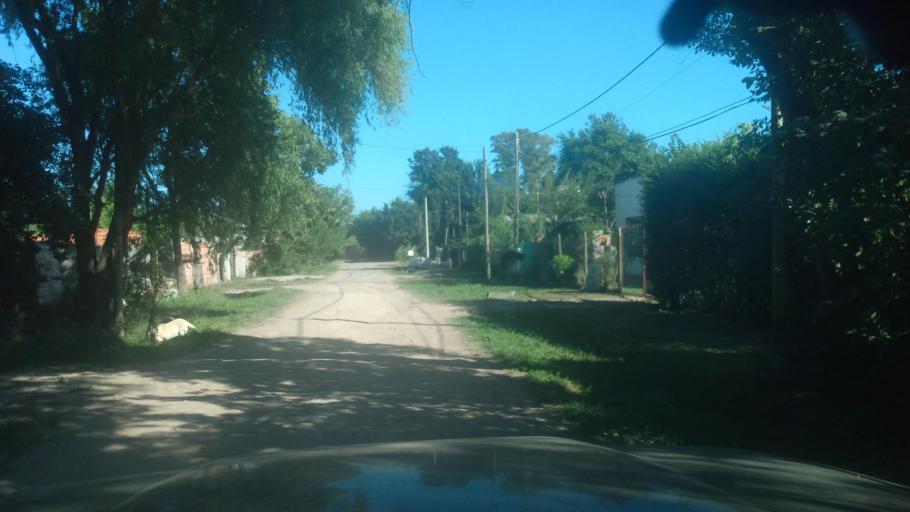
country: AR
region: Buenos Aires
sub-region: Partido de Lujan
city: Lujan
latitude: -34.5855
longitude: -59.0615
